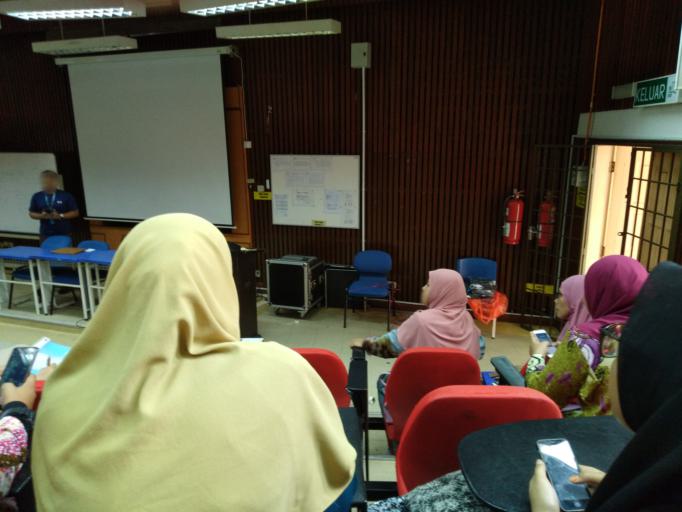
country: MY
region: Perak
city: Ipoh
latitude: 4.5889
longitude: 101.1257
